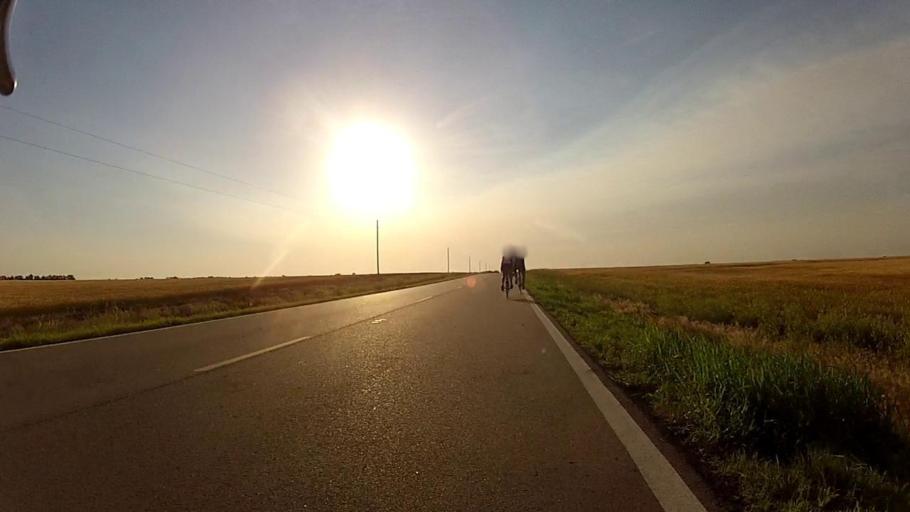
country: US
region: Kansas
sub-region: Harper County
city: Anthony
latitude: 37.1542
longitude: -97.8356
